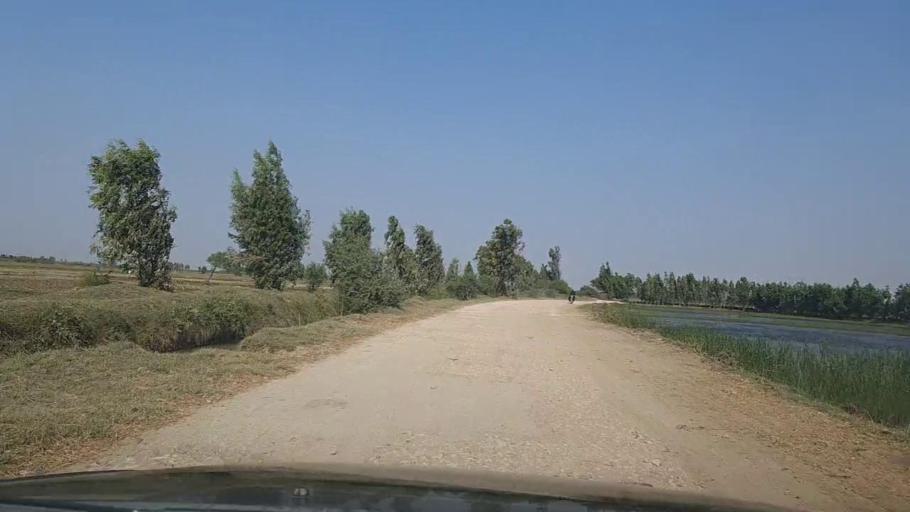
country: PK
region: Sindh
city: Thatta
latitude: 24.6236
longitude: 67.8139
